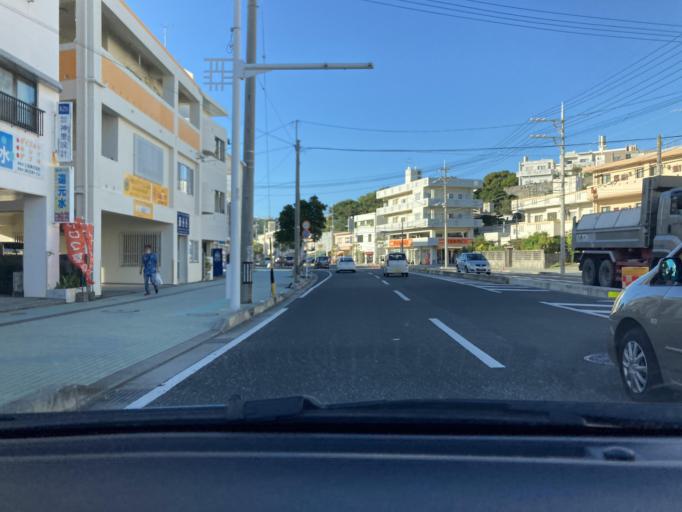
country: JP
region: Okinawa
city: Tomigusuku
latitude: 26.1931
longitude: 127.7280
